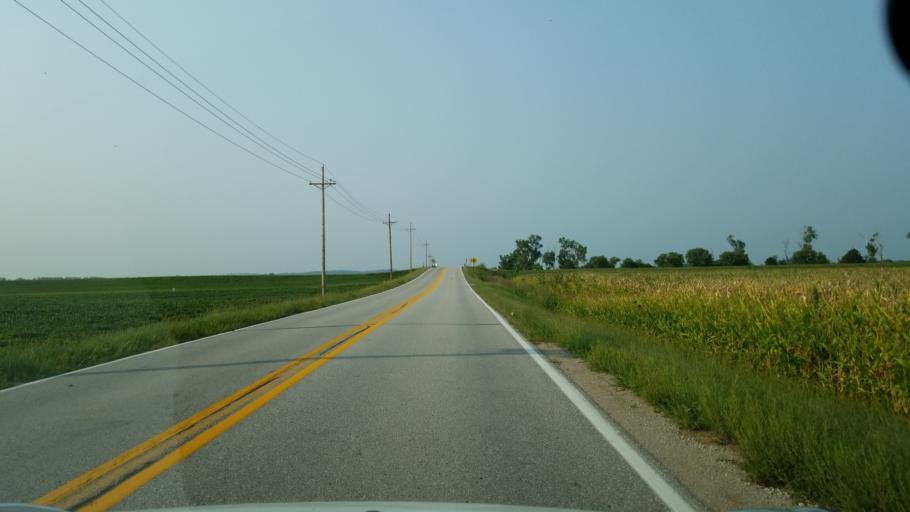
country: US
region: Nebraska
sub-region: Sarpy County
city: Offutt Air Force Base
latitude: 41.0797
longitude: -95.8898
